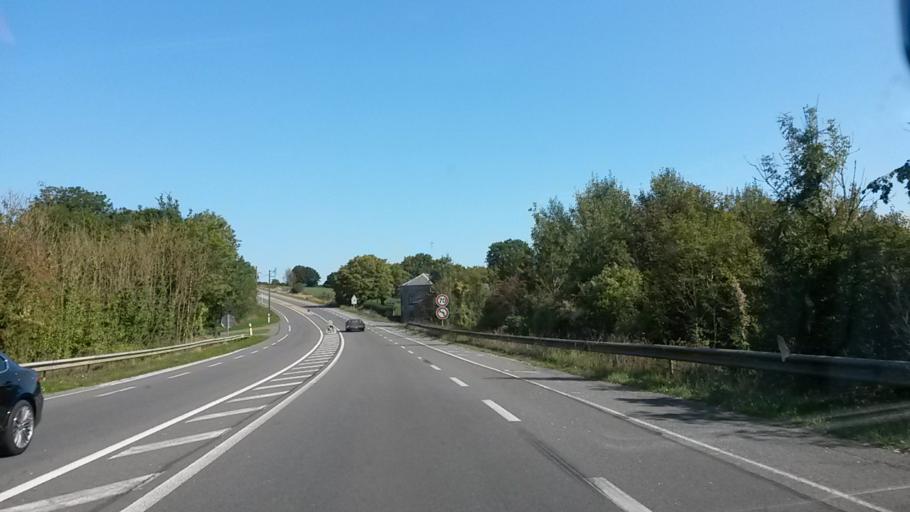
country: FR
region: Nord-Pas-de-Calais
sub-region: Departement du Nord
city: Avesnelles
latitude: 50.1373
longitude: 3.9461
